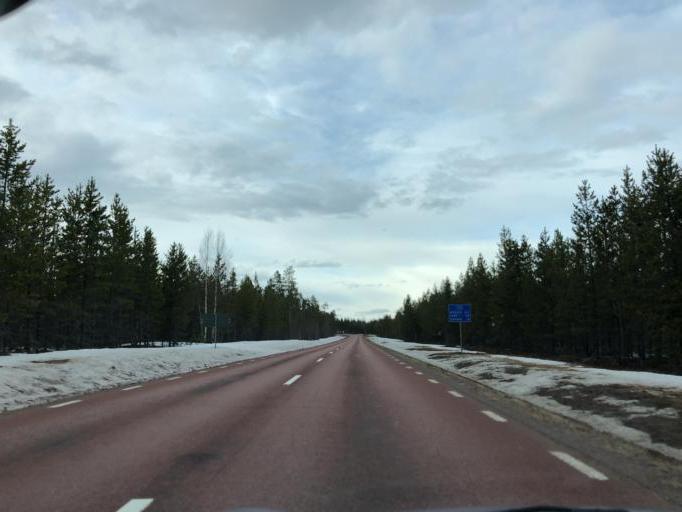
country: SE
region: Dalarna
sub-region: Alvdalens Kommun
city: AElvdalen
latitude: 61.5662
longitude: 13.3096
